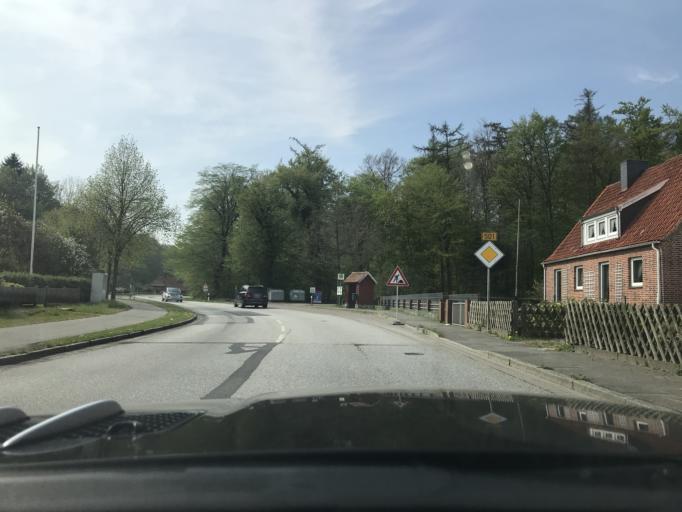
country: DE
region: Schleswig-Holstein
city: Gromitz
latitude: 54.1865
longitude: 10.9813
